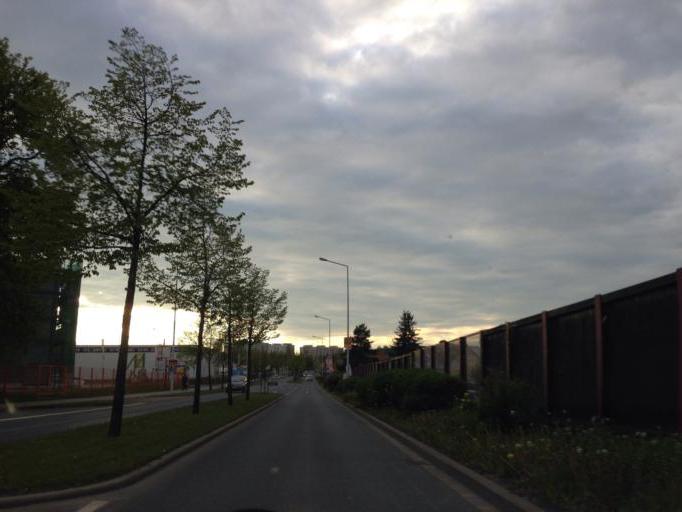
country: DE
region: Saxony
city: Freital
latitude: 51.0128
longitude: 13.6504
